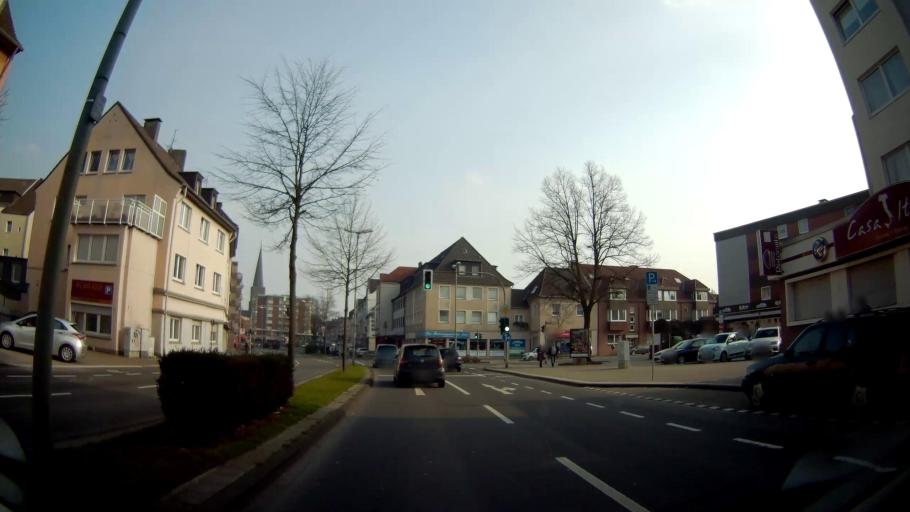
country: DE
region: North Rhine-Westphalia
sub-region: Regierungsbezirk Munster
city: Bottrop
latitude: 51.5192
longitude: 6.9245
